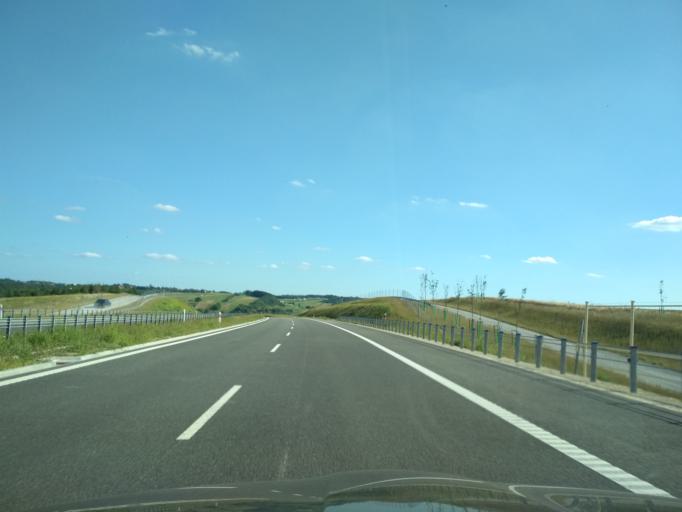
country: PL
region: Subcarpathian Voivodeship
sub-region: Rzeszow
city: Przybyszowka
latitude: 50.0559
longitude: 21.9239
